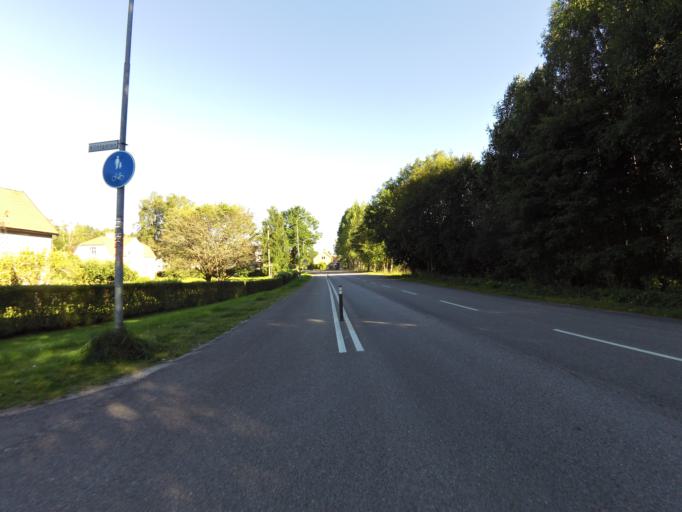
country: SE
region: Gaevleborg
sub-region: Hofors Kommun
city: Hofors
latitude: 60.5697
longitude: 16.2722
